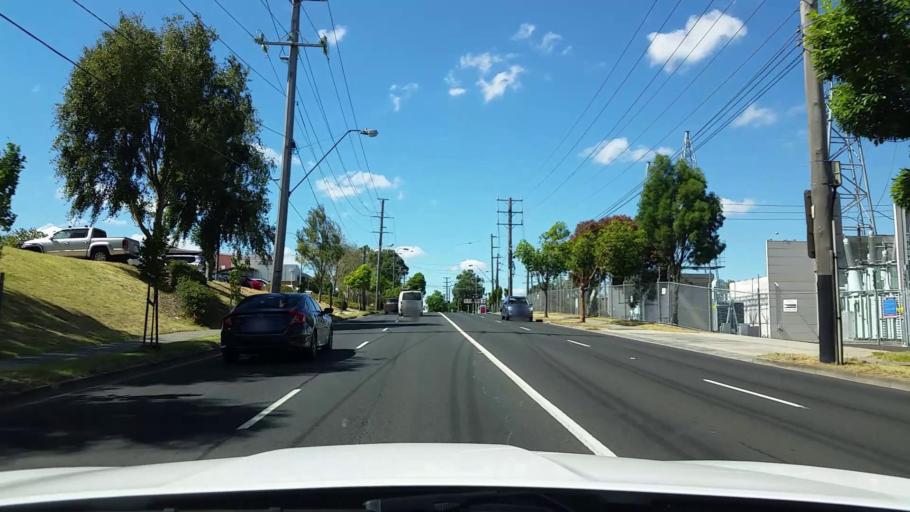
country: AU
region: Victoria
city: Ashburton
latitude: -37.8775
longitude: 145.0832
